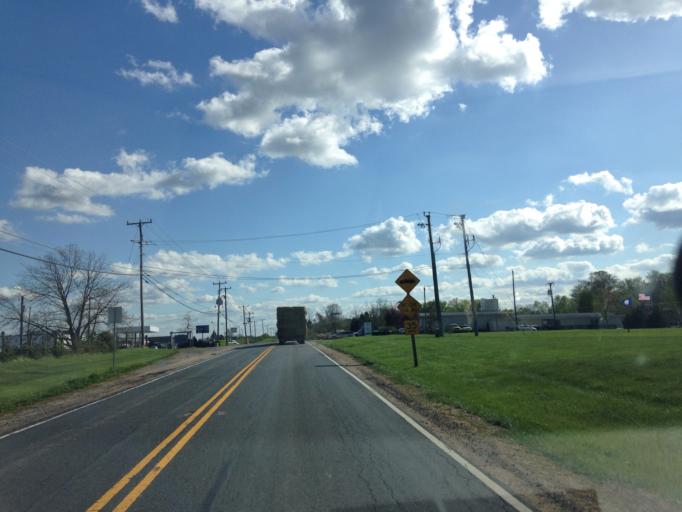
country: US
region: Virginia
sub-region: Loudoun County
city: Lovettsville
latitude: 39.2621
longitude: -77.6431
